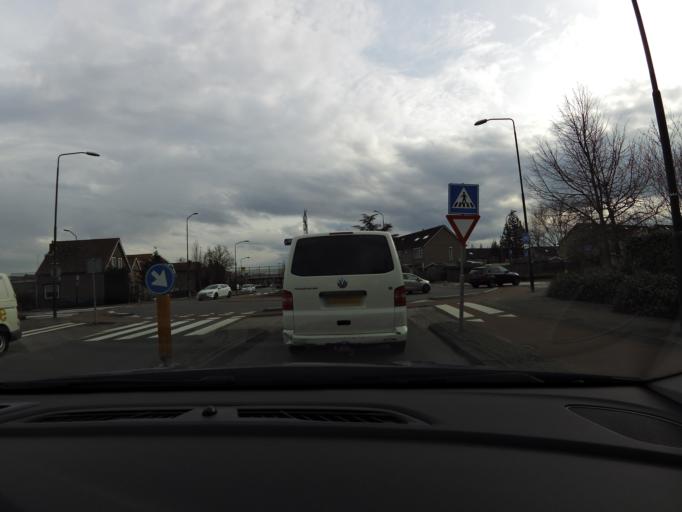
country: NL
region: South Holland
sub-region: Gemeente Hardinxveld-Giessendam
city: Neder-Hardinxveld
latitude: 51.8261
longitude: 4.8447
